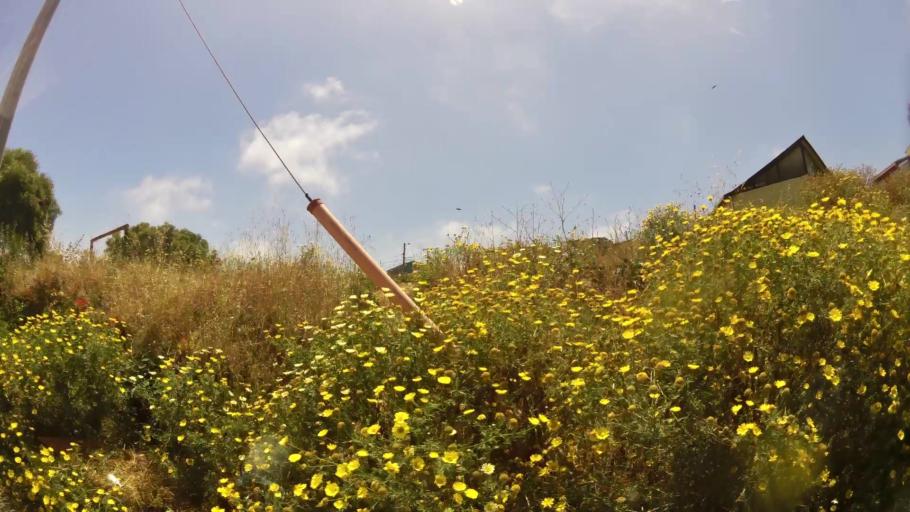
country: CL
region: Valparaiso
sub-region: Provincia de Valparaiso
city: Valparaiso
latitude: -33.0297
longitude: -71.6434
